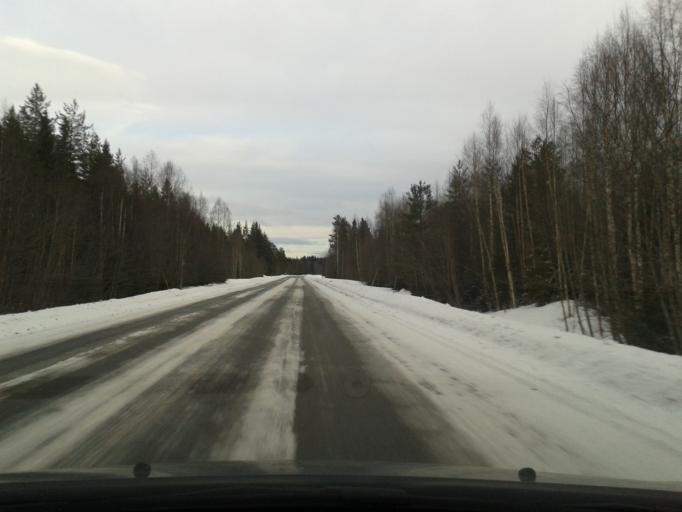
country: SE
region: Vaesternorrland
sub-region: Solleftea Kommun
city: As
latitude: 63.6378
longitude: 16.8061
